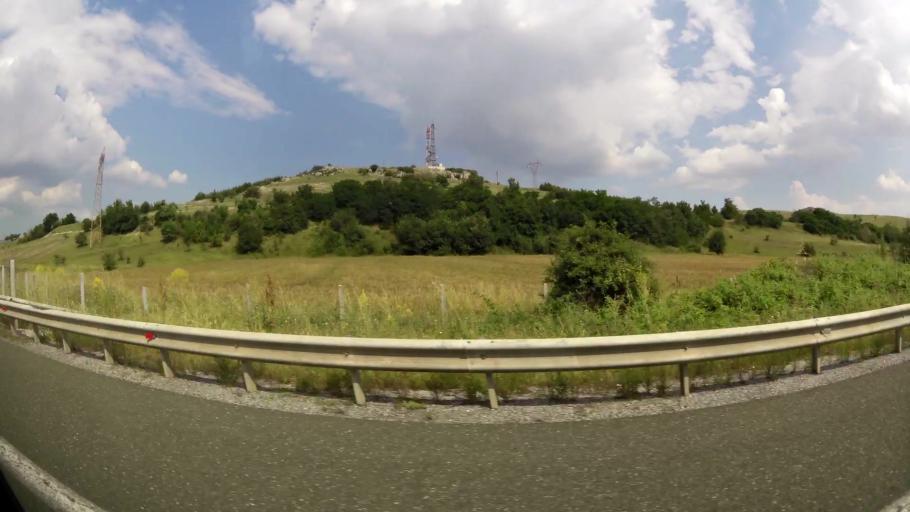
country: GR
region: West Macedonia
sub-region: Nomos Kozanis
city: Koila
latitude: 40.3577
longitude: 21.8148
